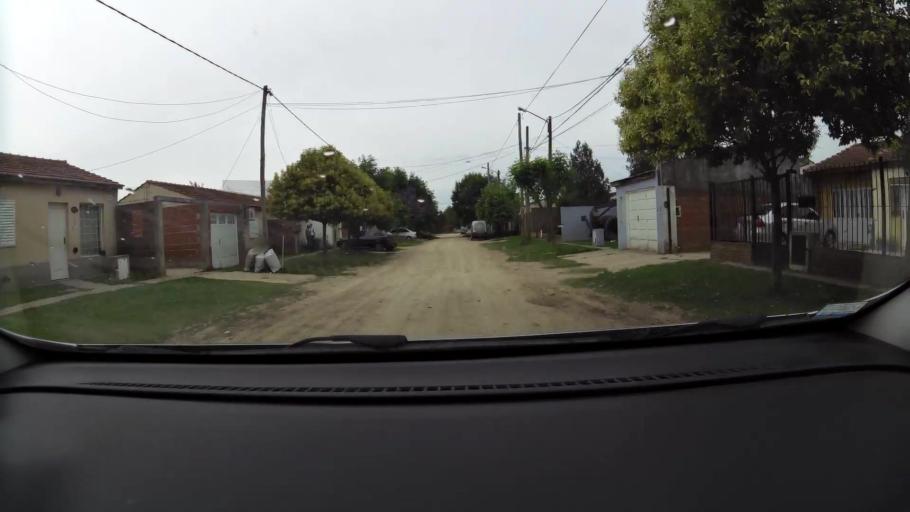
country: AR
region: Buenos Aires
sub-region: Partido de Campana
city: Campana
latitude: -34.2129
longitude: -58.9418
